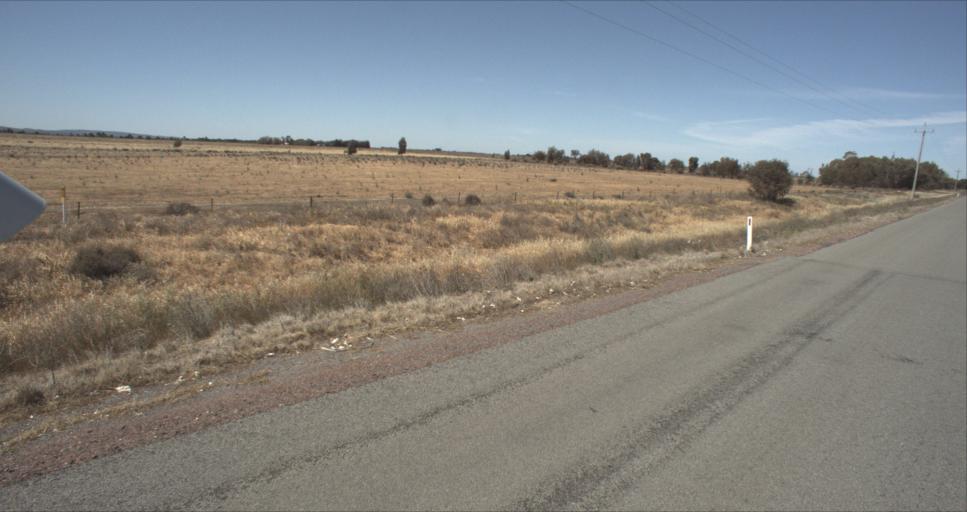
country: AU
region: New South Wales
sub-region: Leeton
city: Leeton
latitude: -34.4333
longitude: 146.2992
